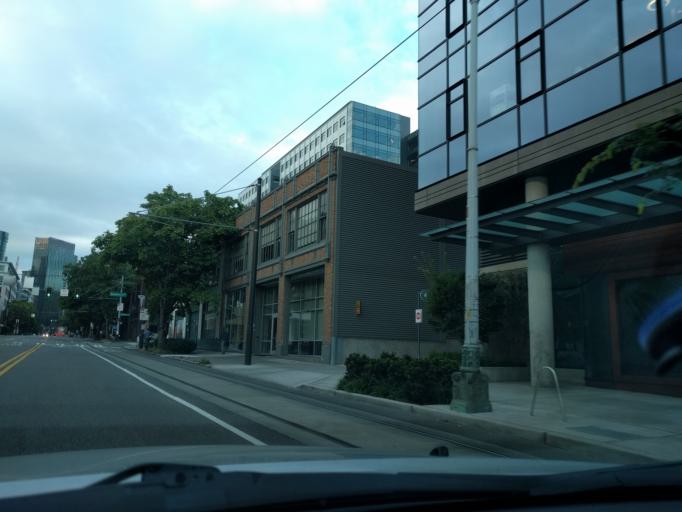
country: US
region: Washington
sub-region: King County
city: Seattle
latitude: 47.6238
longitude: -122.3386
